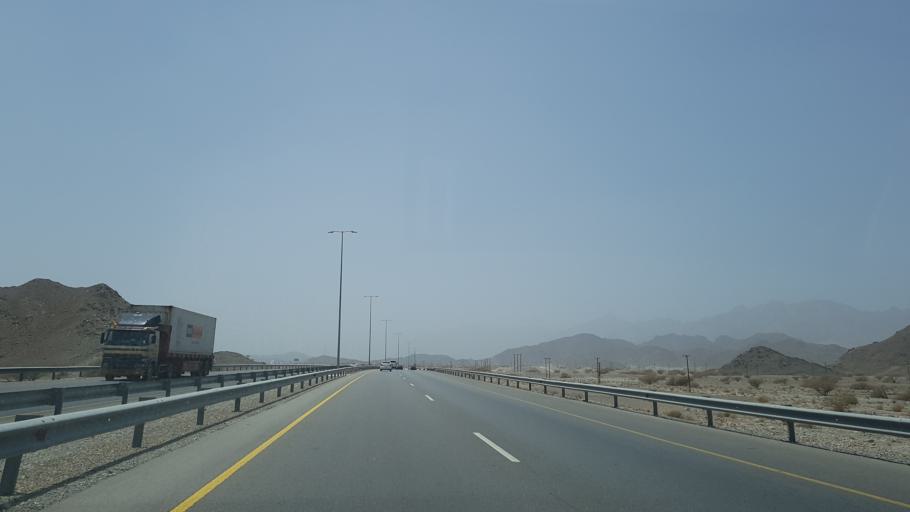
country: OM
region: Muhafazat ad Dakhiliyah
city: Bidbid
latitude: 23.3953
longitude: 58.0705
